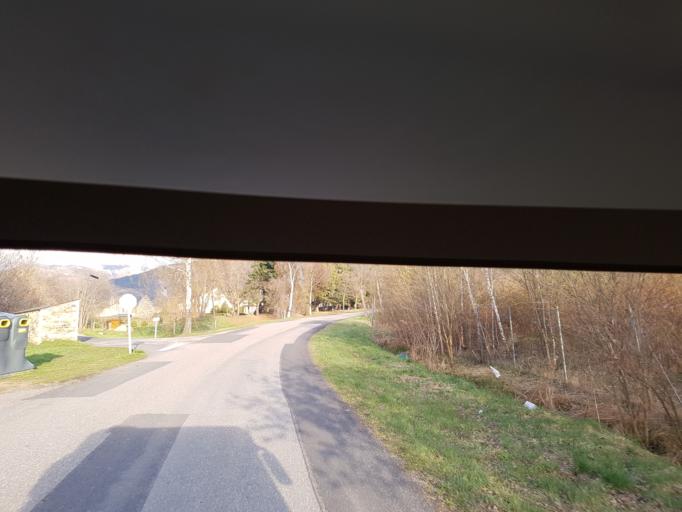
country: ES
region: Catalonia
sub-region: Provincia de Girona
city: Llivia
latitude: 42.4408
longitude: 2.0127
